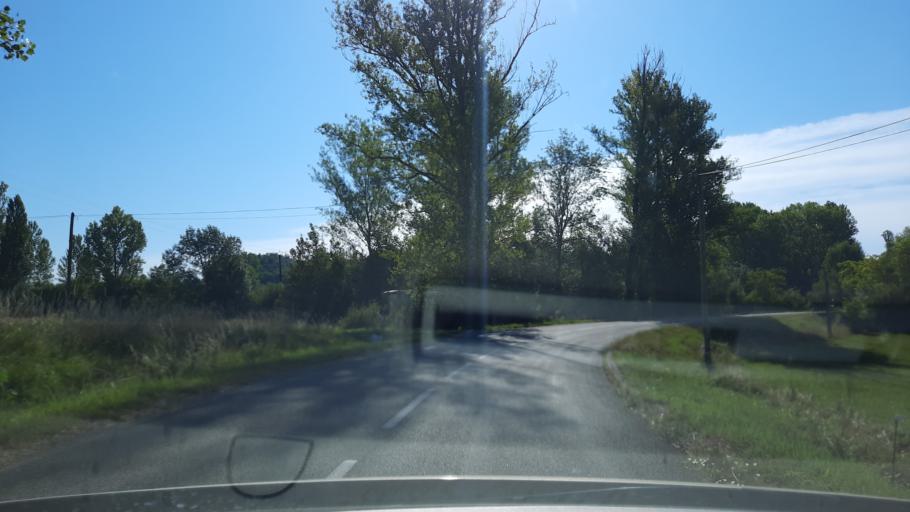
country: FR
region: Midi-Pyrenees
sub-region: Departement du Tarn-et-Garonne
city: Realville
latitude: 44.1918
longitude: 1.4532
